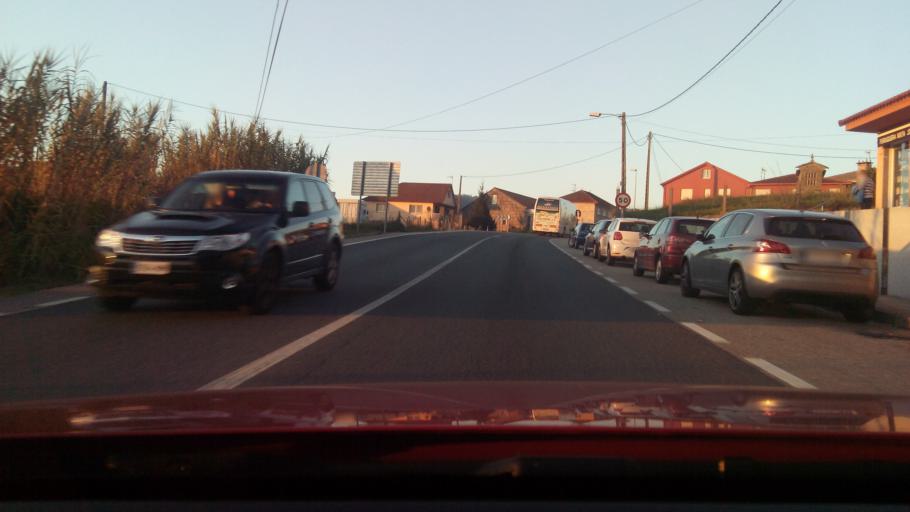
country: ES
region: Galicia
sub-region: Provincia de Pontevedra
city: Gondomar
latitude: 42.1377
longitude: -8.7316
